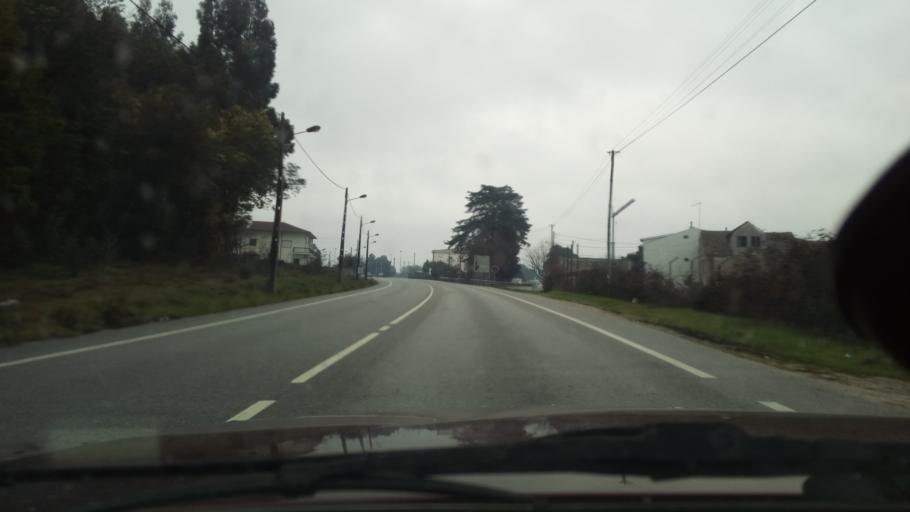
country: PT
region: Viseu
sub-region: Mangualde
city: Mangualde
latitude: 40.6032
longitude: -7.7860
